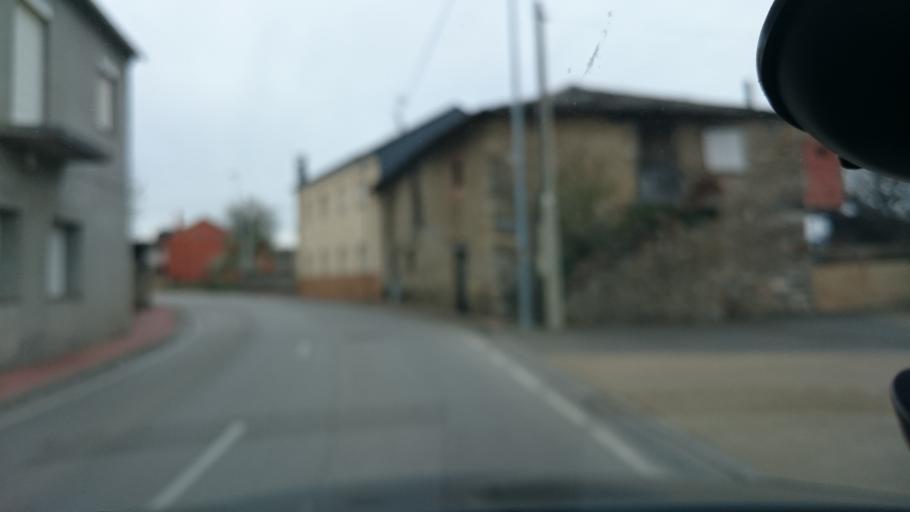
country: ES
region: Castille and Leon
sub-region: Provincia de Leon
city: Carracedelo
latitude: 42.5504
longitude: -6.7365
